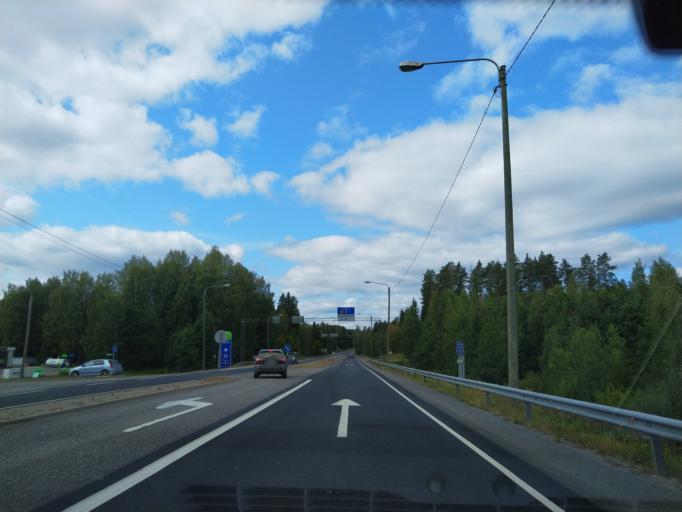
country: FI
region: Haeme
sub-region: Riihimaeki
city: Loppi
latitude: 60.7218
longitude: 24.4444
